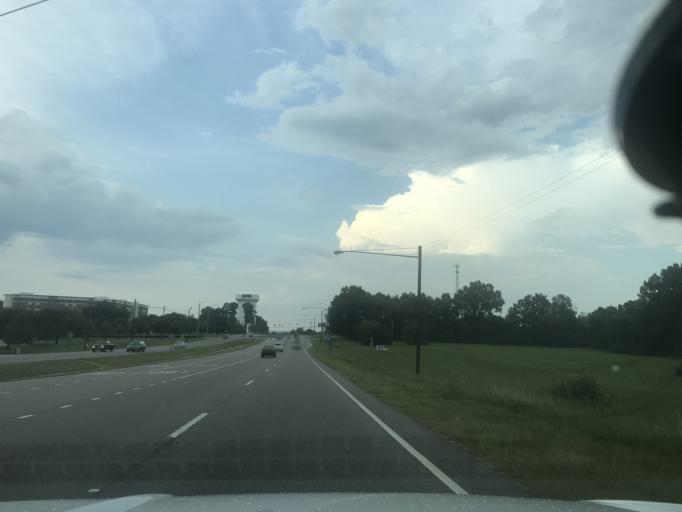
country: US
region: Alabama
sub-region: Montgomery County
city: Pike Road
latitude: 32.3655
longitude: -86.1712
